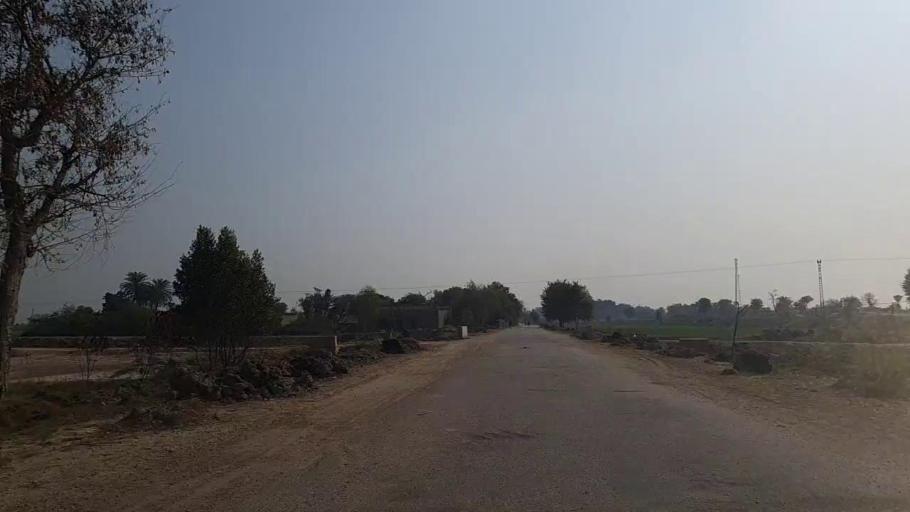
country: PK
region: Sindh
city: Jam Sahib
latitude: 26.3368
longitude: 68.5354
